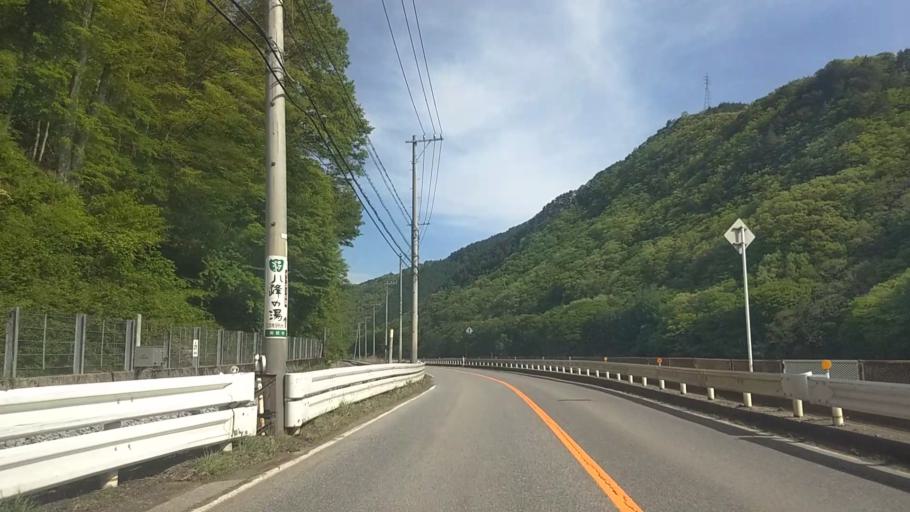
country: JP
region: Nagano
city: Saku
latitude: 36.0299
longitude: 138.4863
